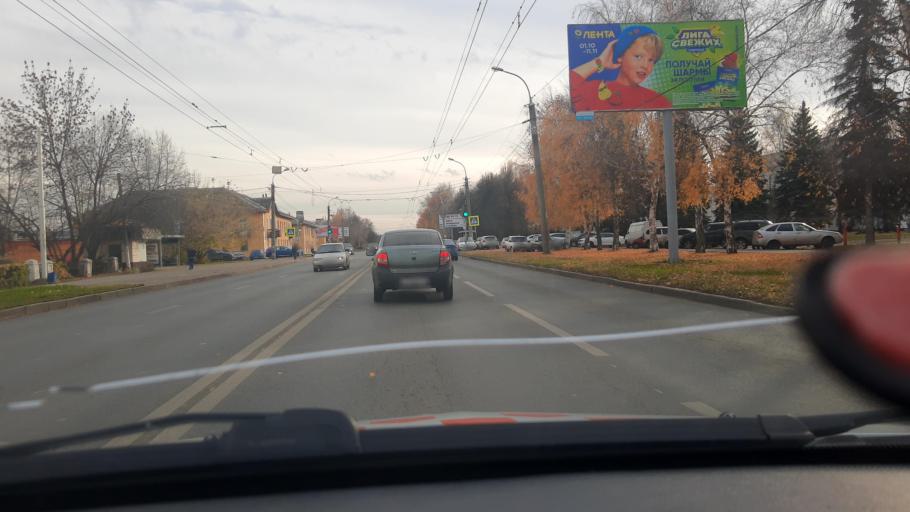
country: RU
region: Bashkortostan
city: Ufa
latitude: 54.7937
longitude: 56.1392
